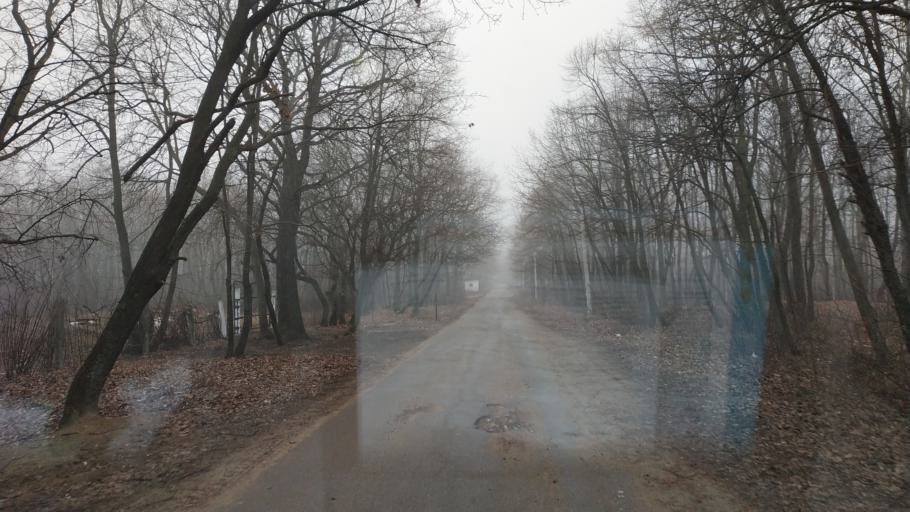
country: MD
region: Laloveni
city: Ialoveni
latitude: 46.9525
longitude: 28.6986
